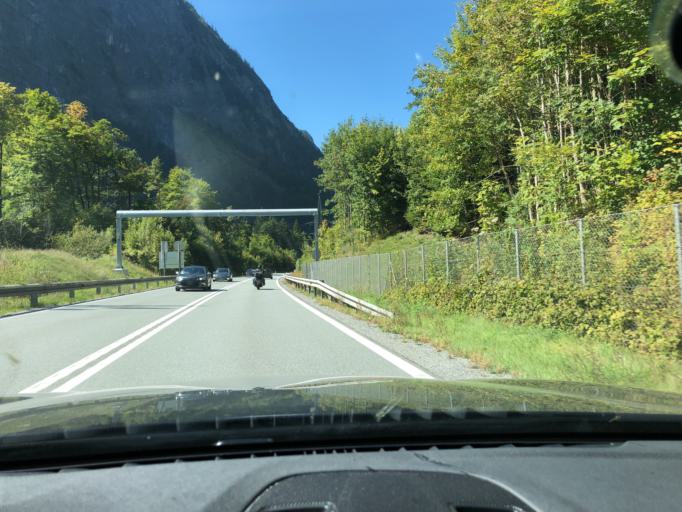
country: AT
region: Vorarlberg
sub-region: Politischer Bezirk Bludenz
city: Dalaas
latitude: 47.1295
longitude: 9.9660
